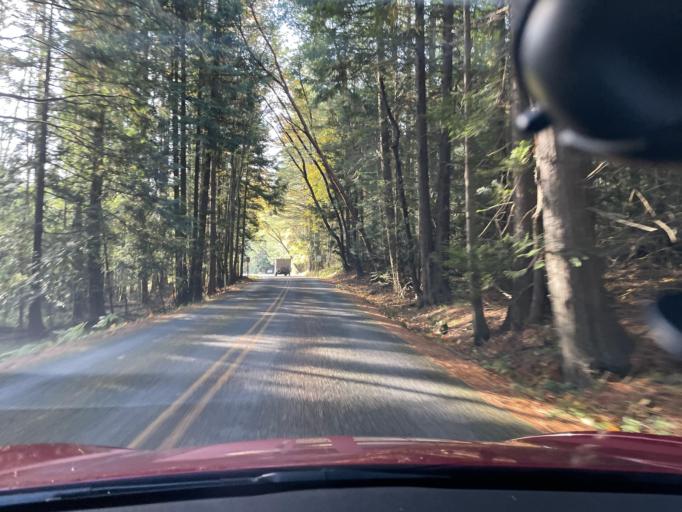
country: US
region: Washington
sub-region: San Juan County
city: Friday Harbor
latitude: 48.5243
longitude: -123.1458
